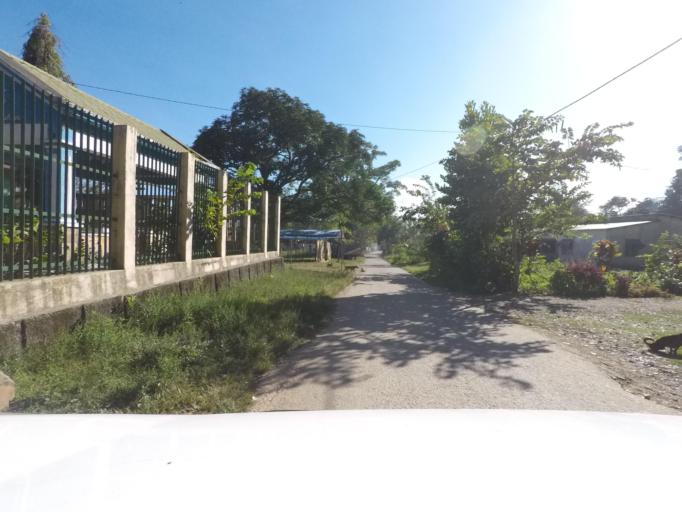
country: TL
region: Ermera
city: Gleno
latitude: -8.7308
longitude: 125.4325
